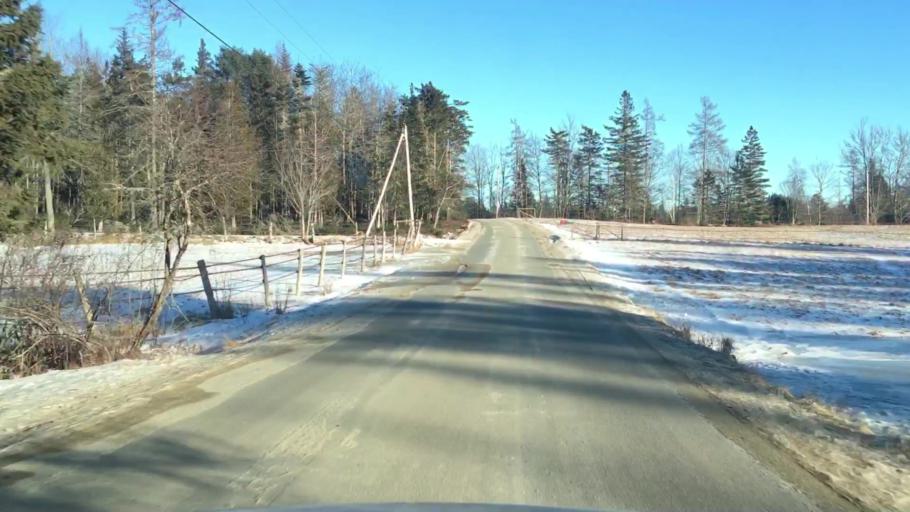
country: US
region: Maine
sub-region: Hancock County
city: Castine
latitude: 44.3822
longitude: -68.7279
